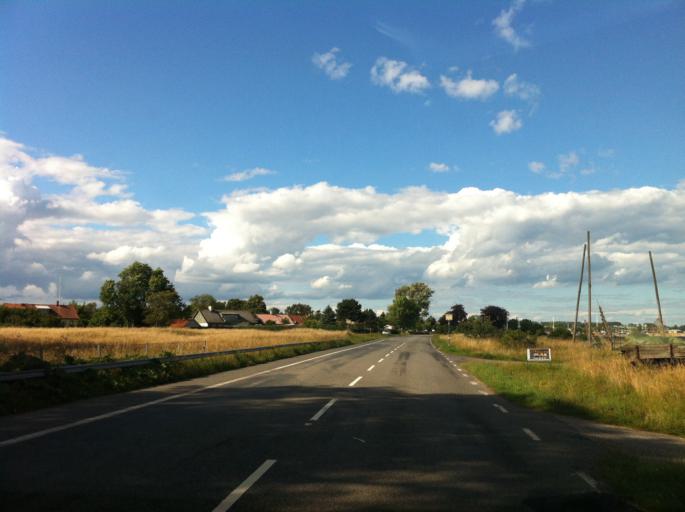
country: SE
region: Skane
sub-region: Simrishamns Kommun
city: Simrishamn
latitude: 55.4588
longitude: 14.2723
